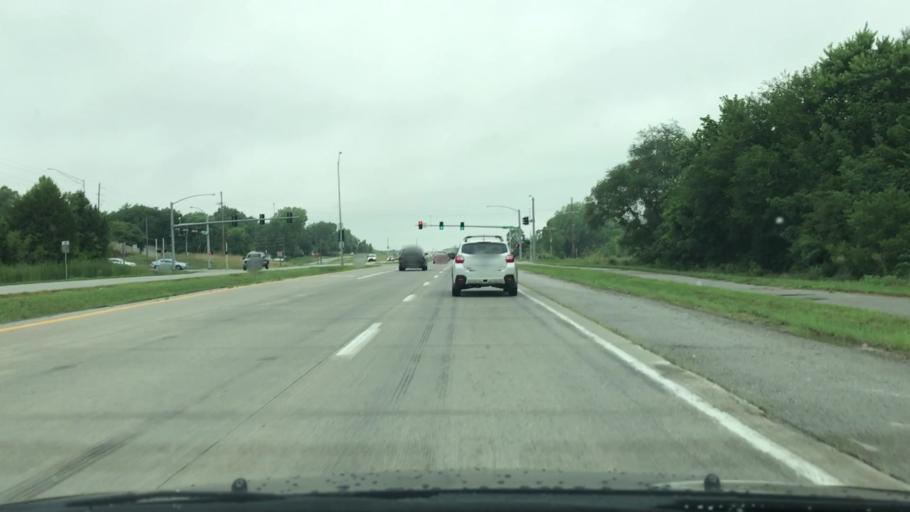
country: US
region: Missouri
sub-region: Jackson County
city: Grandview
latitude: 38.8579
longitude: -94.5157
